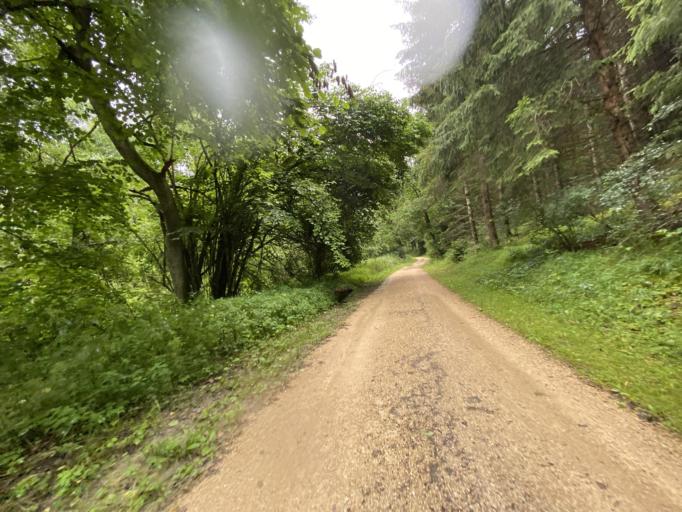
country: DE
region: Baden-Wuerttemberg
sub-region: Tuebingen Region
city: Sigmaringen
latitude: 48.1137
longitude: 9.2194
